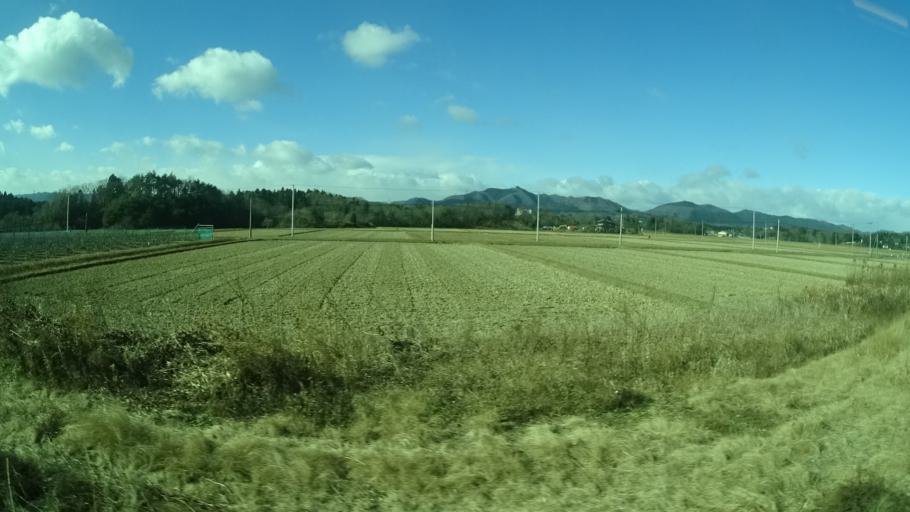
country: JP
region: Miyagi
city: Marumori
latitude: 37.8559
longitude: 140.9302
